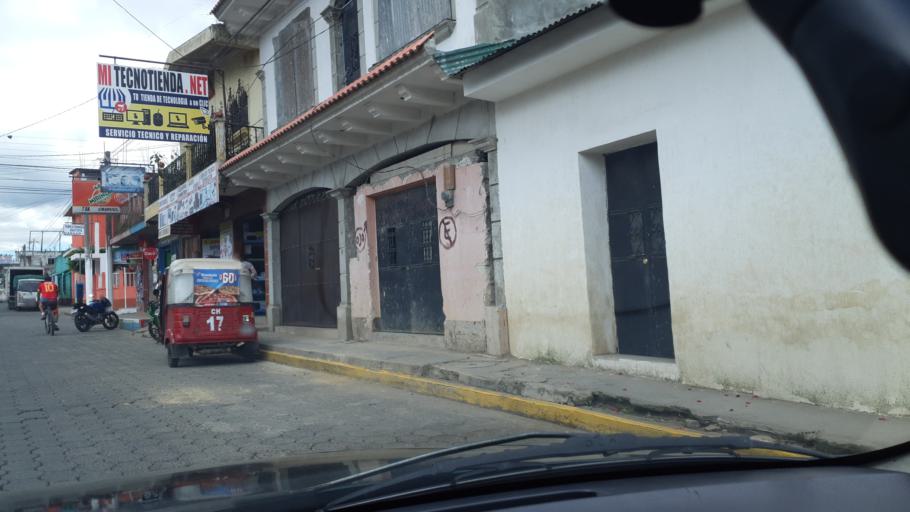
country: GT
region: Chimaltenango
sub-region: Municipio de Chimaltenango
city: Chimaltenango
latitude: 14.6617
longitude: -90.8229
